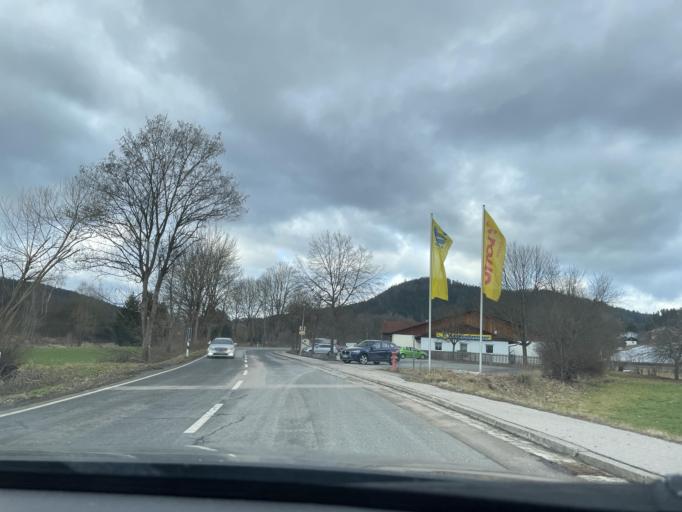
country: DE
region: Bavaria
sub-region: Upper Palatinate
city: Blaibach
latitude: 49.1647
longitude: 12.8073
